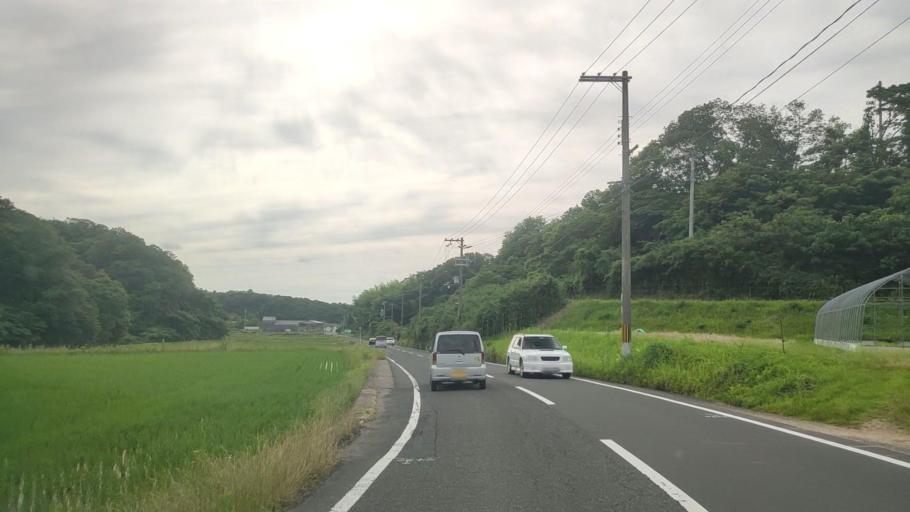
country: JP
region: Kyoto
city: Miyazu
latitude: 35.6832
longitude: 135.0659
